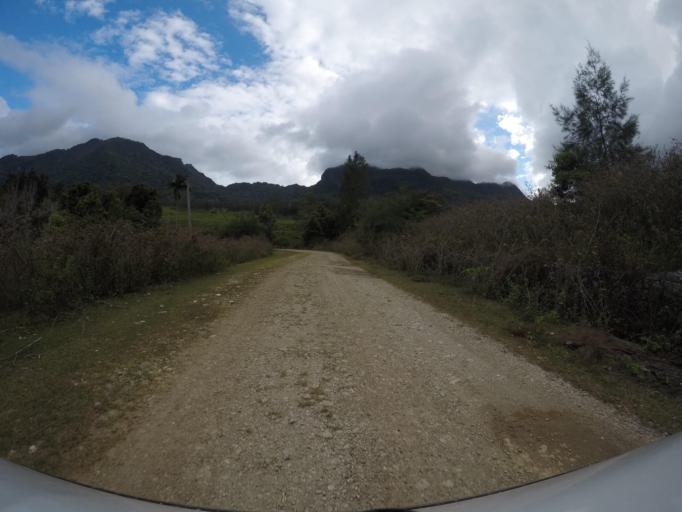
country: TL
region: Baucau
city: Venilale
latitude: -8.6807
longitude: 126.6366
